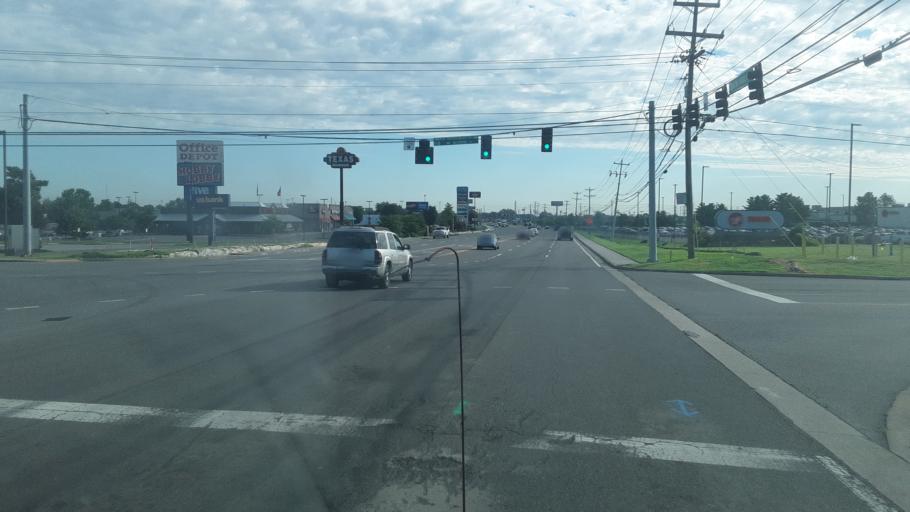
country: US
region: Tennessee
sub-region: Montgomery County
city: Clarksville
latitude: 36.5818
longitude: -87.2974
